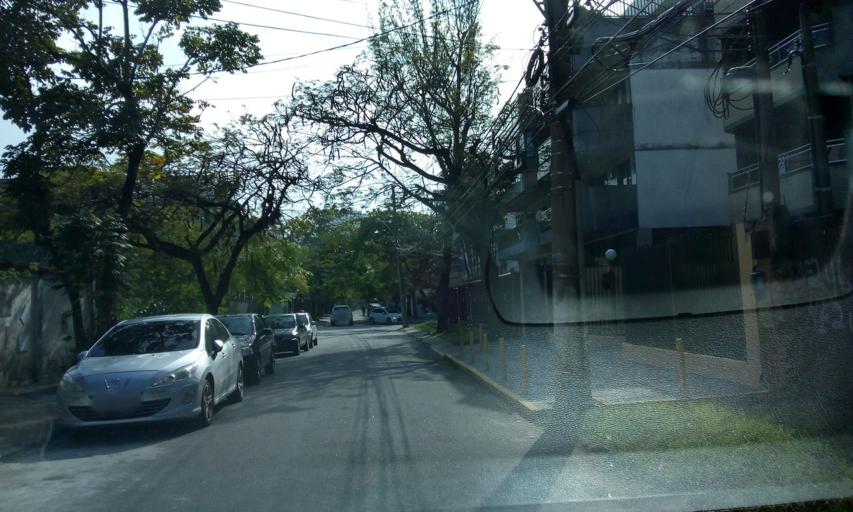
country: BR
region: Rio de Janeiro
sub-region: Nilopolis
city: Nilopolis
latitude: -23.0116
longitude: -43.4459
